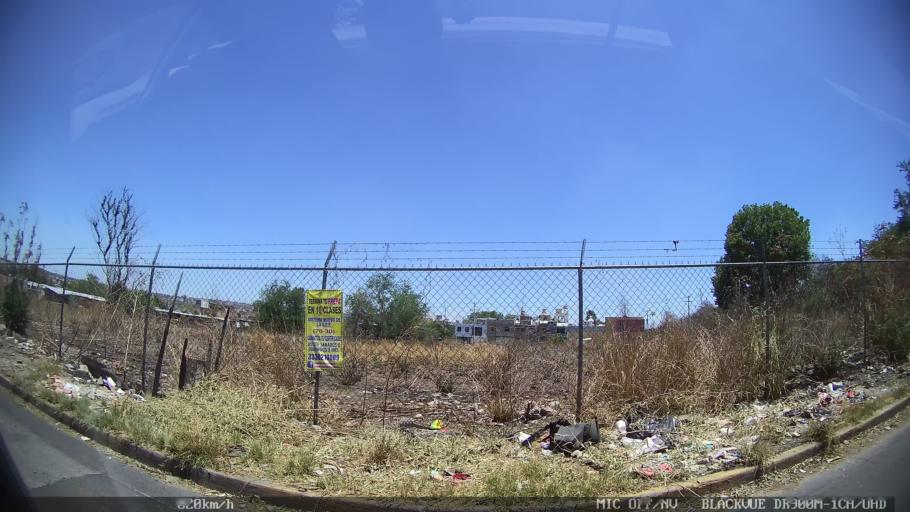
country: MX
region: Jalisco
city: Tlaquepaque
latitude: 20.6477
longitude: -103.2764
